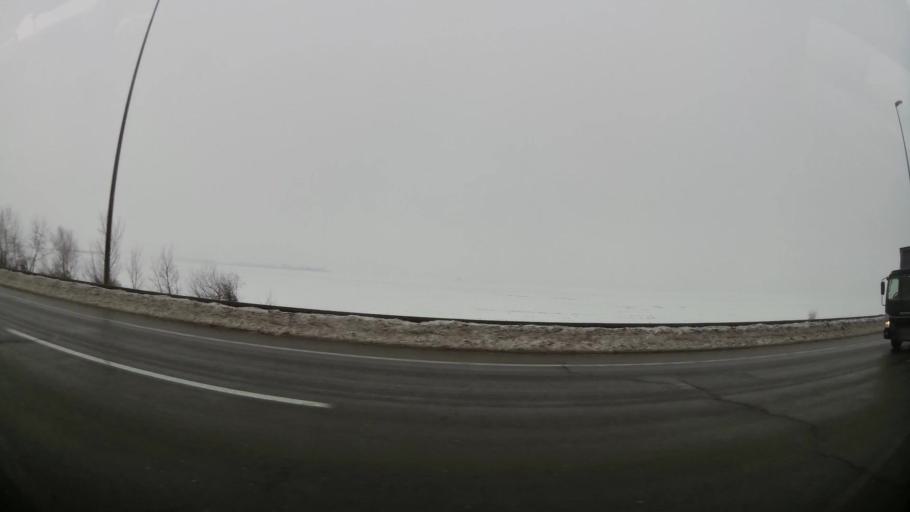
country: RS
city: Dobanovci
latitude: 44.8242
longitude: 20.2521
